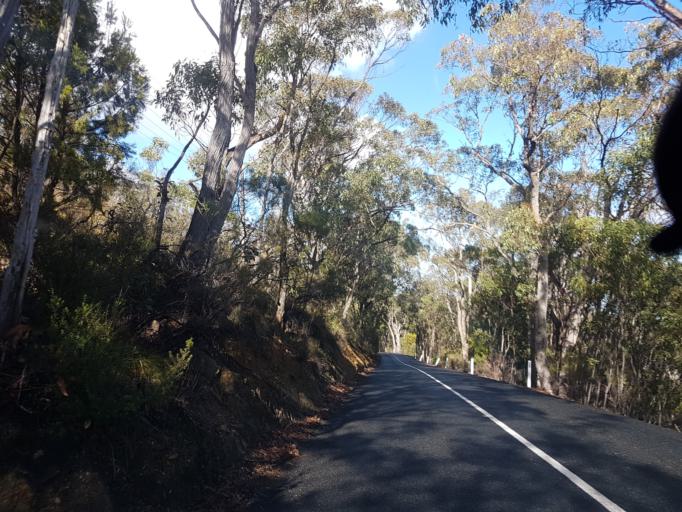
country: AU
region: South Australia
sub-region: Adelaide Hills
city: Heathfield
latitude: -35.0304
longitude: 138.7135
